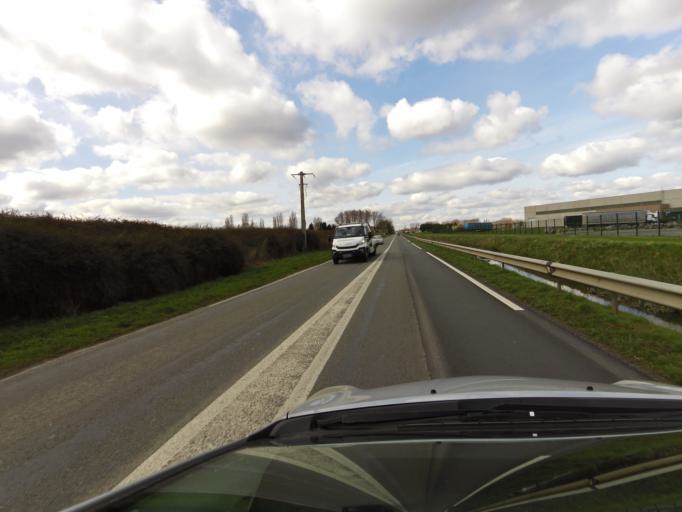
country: FR
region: Nord-Pas-de-Calais
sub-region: Departement du Pas-de-Calais
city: Lorgies
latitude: 50.5583
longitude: 2.7880
